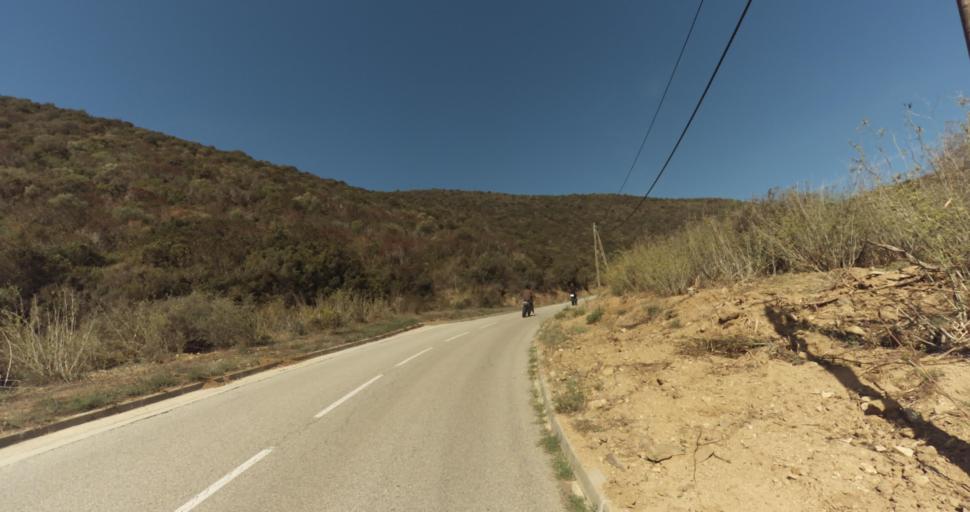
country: FR
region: Corsica
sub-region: Departement de la Corse-du-Sud
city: Ajaccio
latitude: 41.9159
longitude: 8.6431
